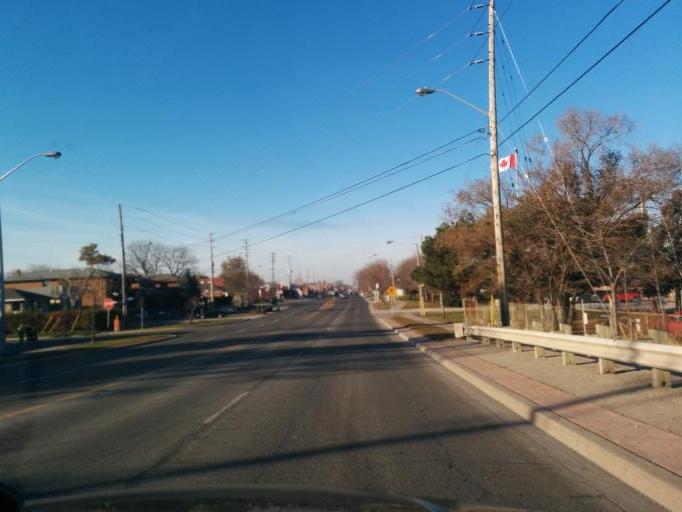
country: CA
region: Ontario
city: Etobicoke
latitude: 43.5952
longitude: -79.5422
